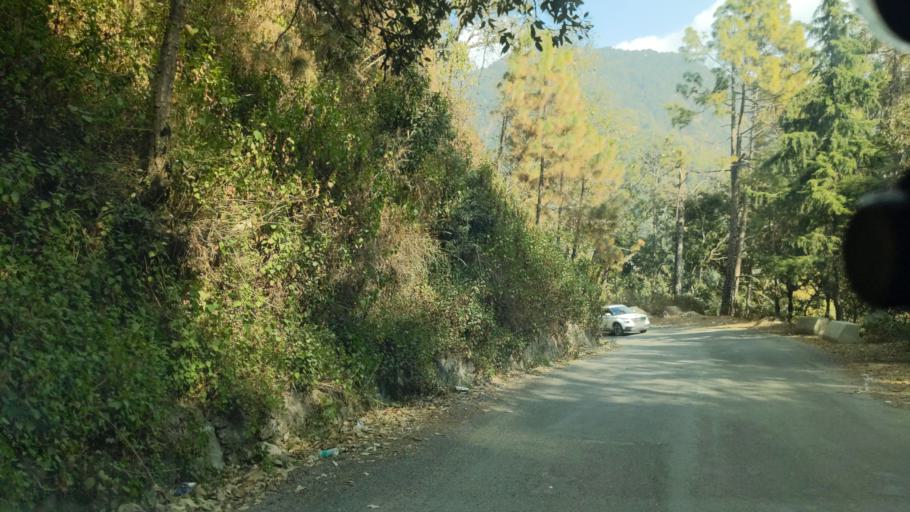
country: IN
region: Uttarakhand
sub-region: Naini Tal
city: Bhowali
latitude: 29.4053
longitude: 79.5375
